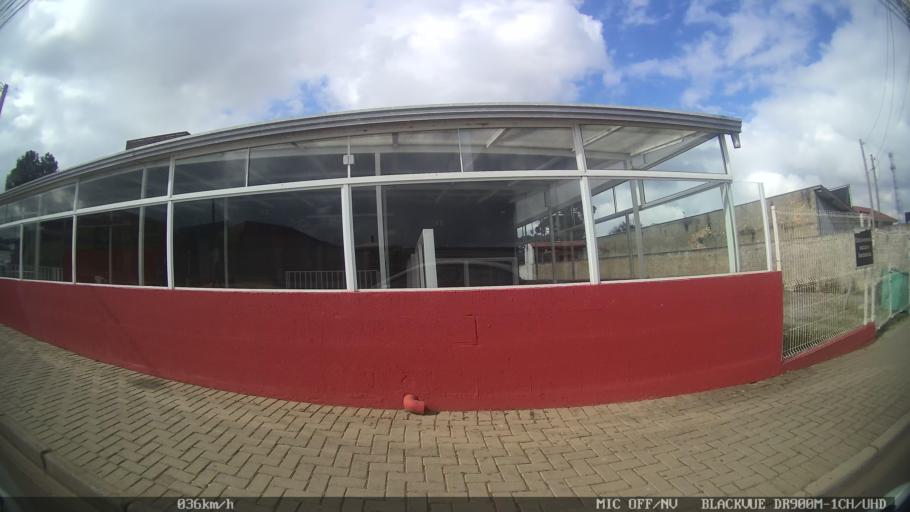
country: BR
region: Parana
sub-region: Colombo
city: Colombo
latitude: -25.3567
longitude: -49.2007
